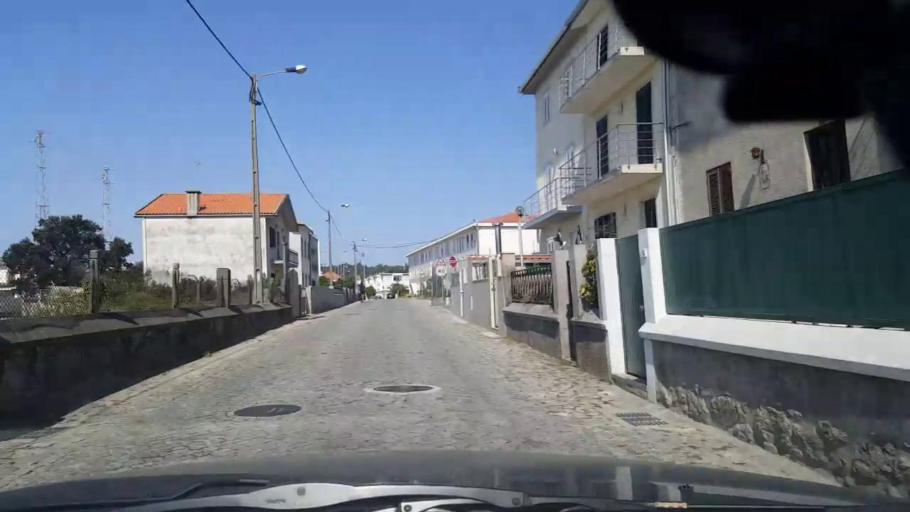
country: PT
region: Porto
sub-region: Vila do Conde
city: Vila do Conde
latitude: 41.3596
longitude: -8.7274
